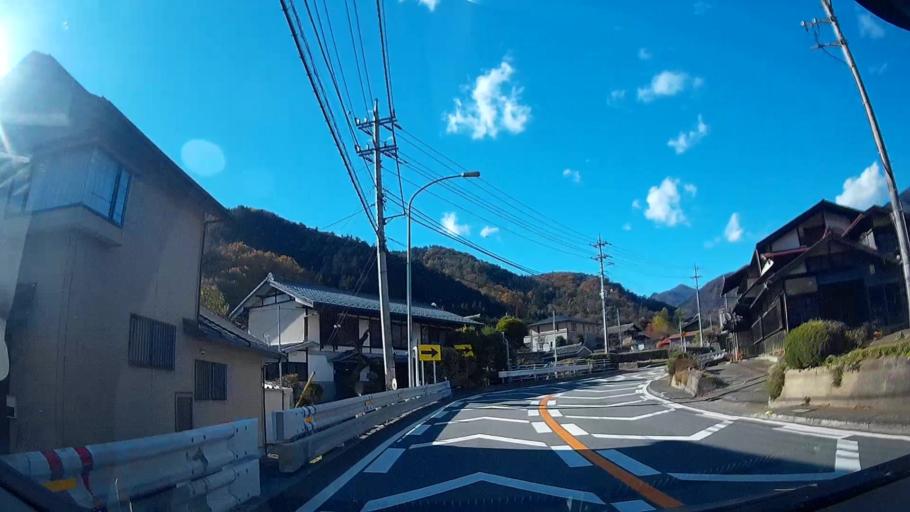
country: JP
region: Yamanashi
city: Otsuki
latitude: 35.5965
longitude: 138.8742
